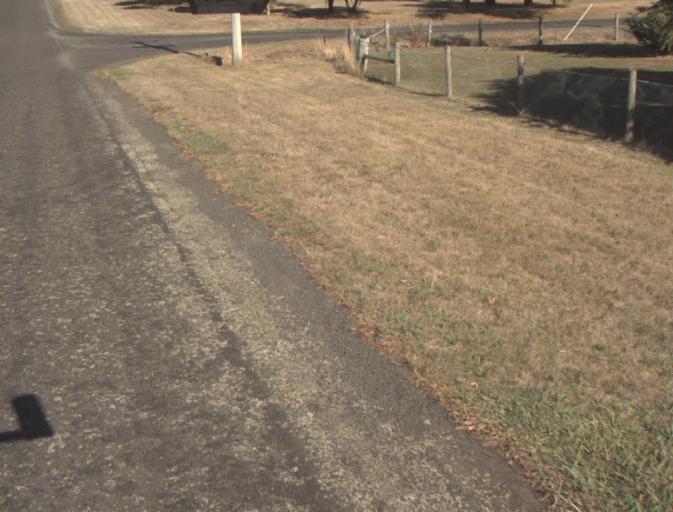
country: AU
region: Tasmania
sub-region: Launceston
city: Mayfield
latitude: -41.3265
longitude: 147.0567
